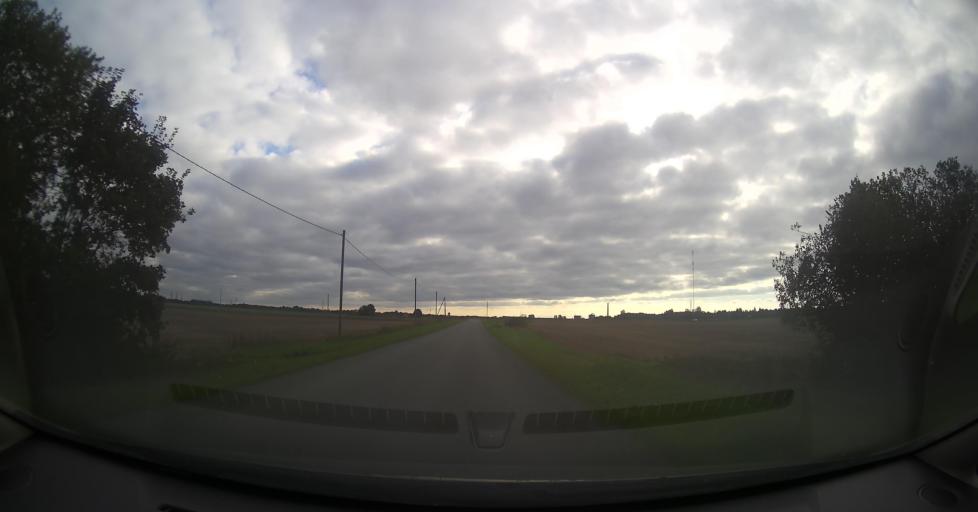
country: EE
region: Harju
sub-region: Anija vald
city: Kehra
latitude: 59.3522
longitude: 25.3035
